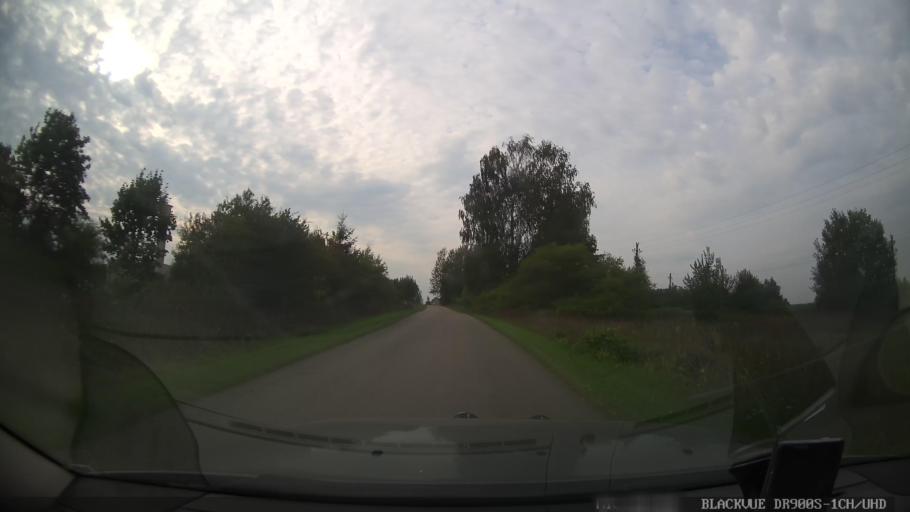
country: LT
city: Skaidiskes
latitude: 54.5367
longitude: 25.6547
